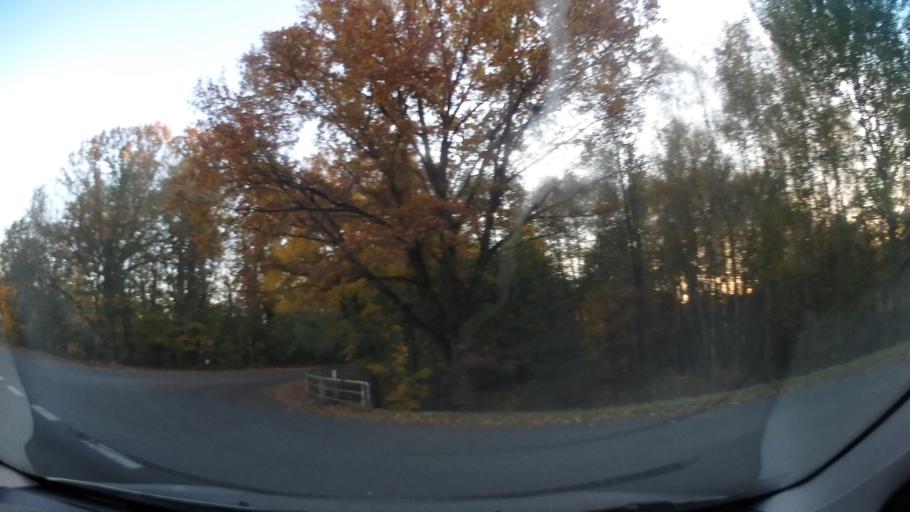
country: CZ
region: Pardubicky
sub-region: Okres Pardubice
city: Lazne Bohdanec
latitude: 50.0858
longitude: 15.6673
